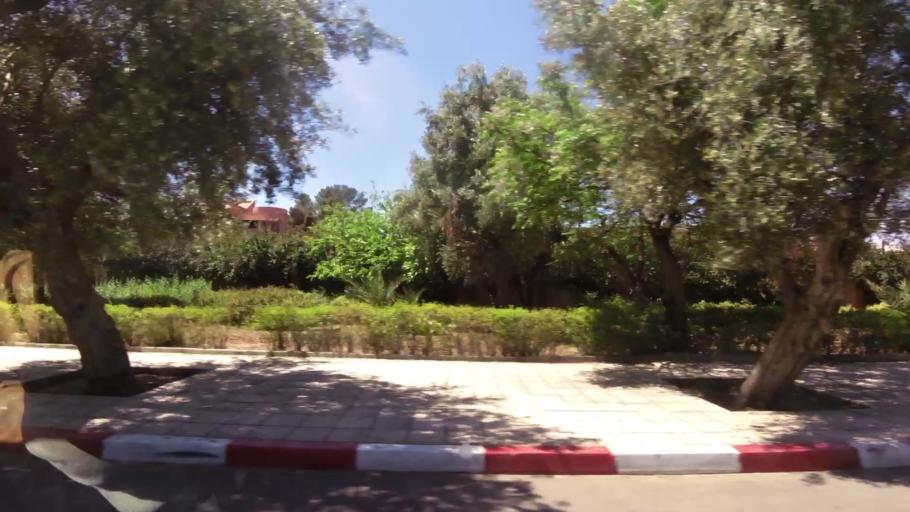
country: MA
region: Marrakech-Tensift-Al Haouz
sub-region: Marrakech
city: Marrakesh
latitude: 31.6283
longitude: -8.0113
